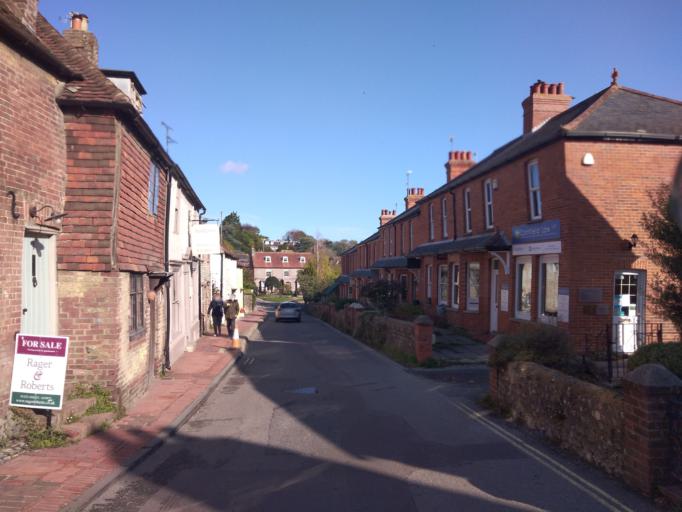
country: GB
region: England
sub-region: East Sussex
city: Seaford
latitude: 50.8084
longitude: 0.1568
